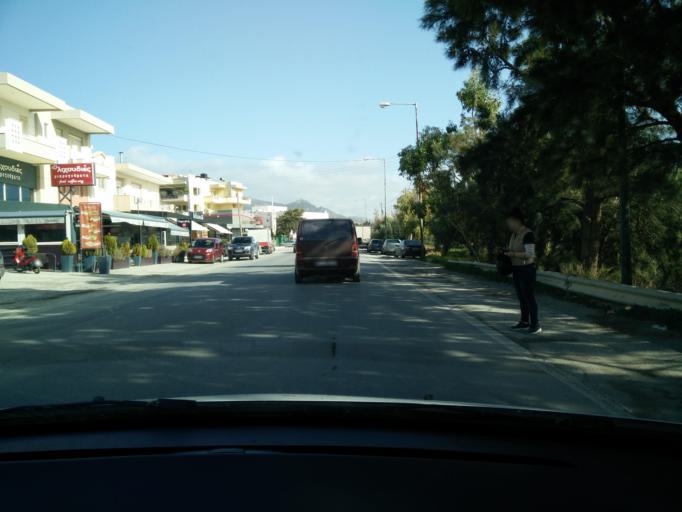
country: GR
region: Crete
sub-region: Nomos Lasithiou
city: Ierapetra
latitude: 35.0154
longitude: 25.7422
